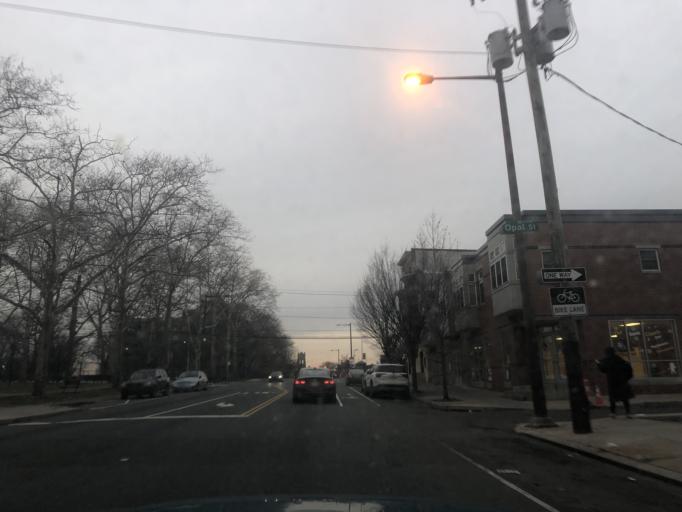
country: US
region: Pennsylvania
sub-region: Philadelphia County
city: Philadelphia
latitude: 39.9951
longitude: -75.1633
